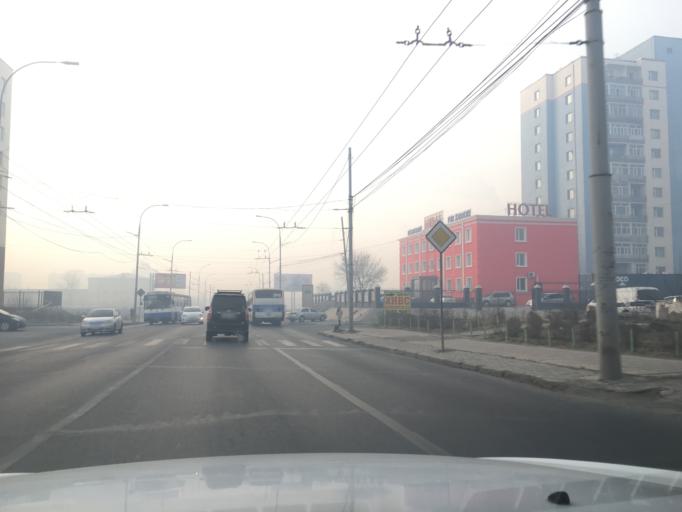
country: MN
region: Ulaanbaatar
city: Ulaanbaatar
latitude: 47.9160
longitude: 106.8183
